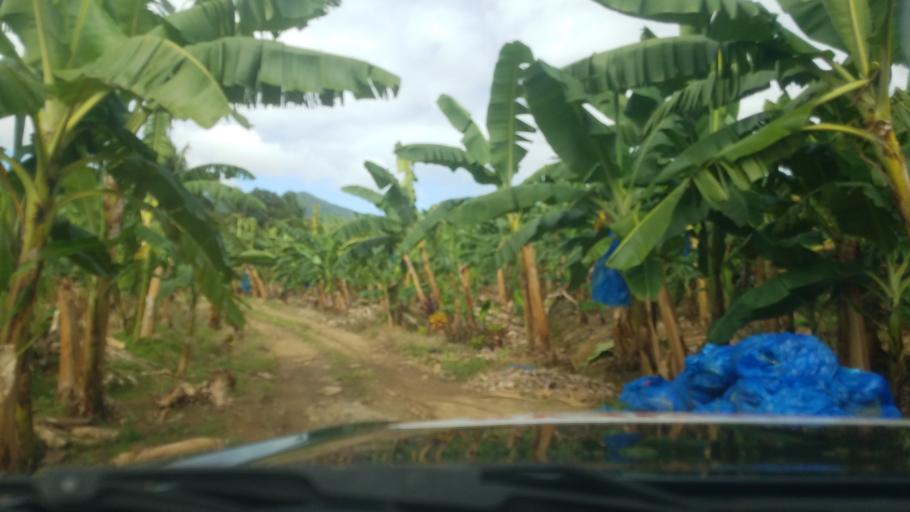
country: LC
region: Dennery Quarter
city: Dennery
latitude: 13.9316
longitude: -60.9246
